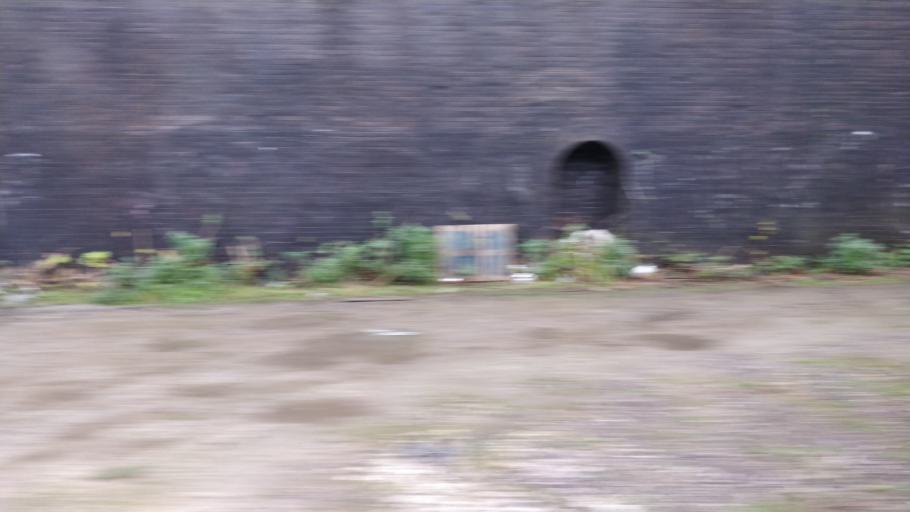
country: GB
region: England
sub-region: City and Borough of Salford
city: Salford
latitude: 53.4929
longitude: -2.2847
